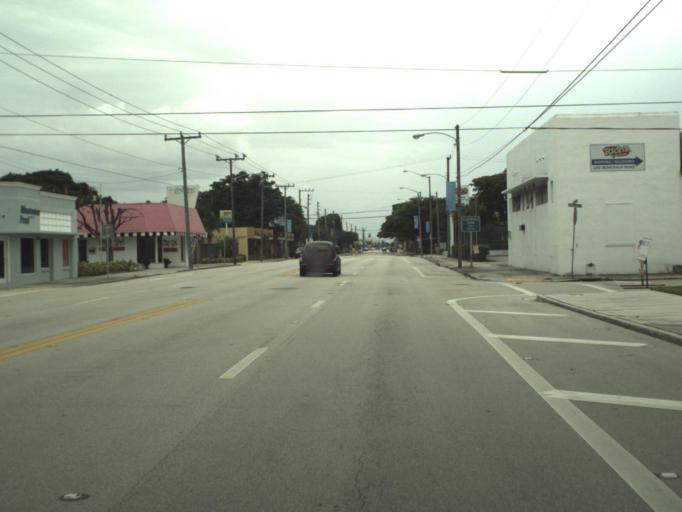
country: US
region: Florida
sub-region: Palm Beach County
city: Palm Beach
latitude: 26.6879
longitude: -80.0545
